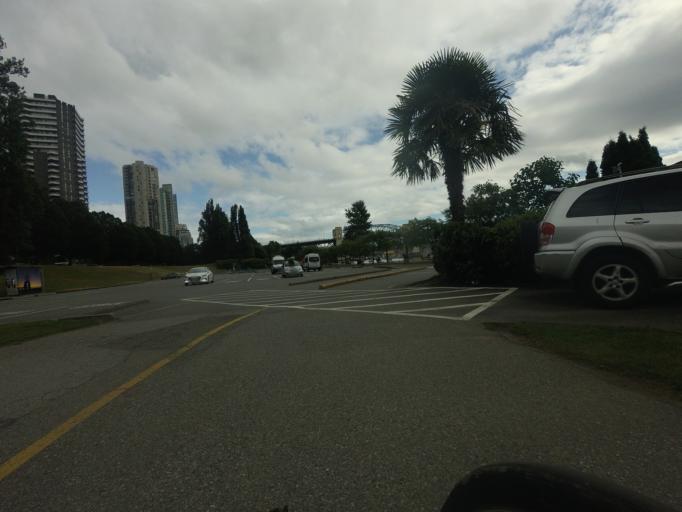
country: CA
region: British Columbia
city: West End
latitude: 49.2788
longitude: -123.1376
